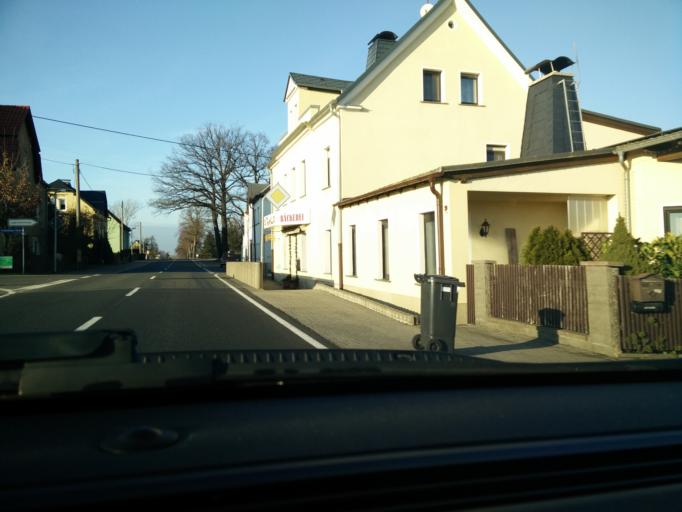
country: DE
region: Saxony
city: Bad Lausick
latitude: 51.1254
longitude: 12.6625
